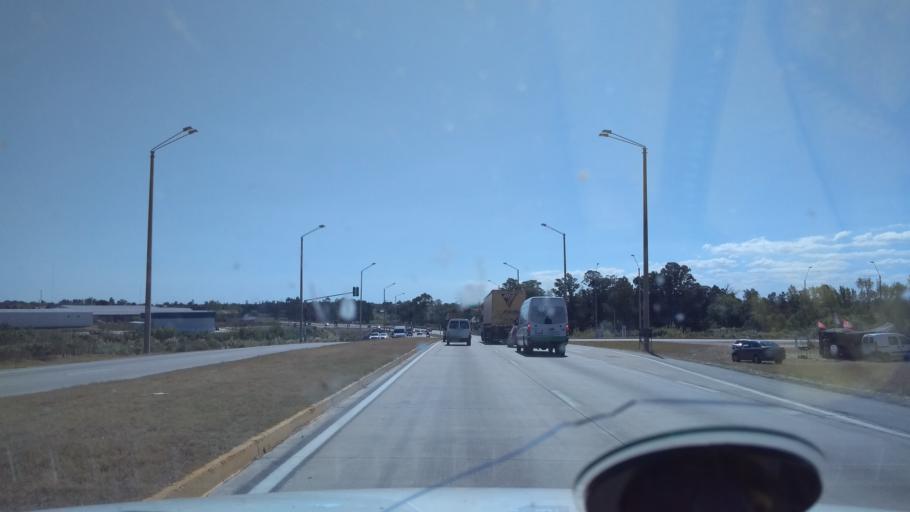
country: UY
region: Canelones
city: Toledo
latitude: -34.7908
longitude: -56.1054
